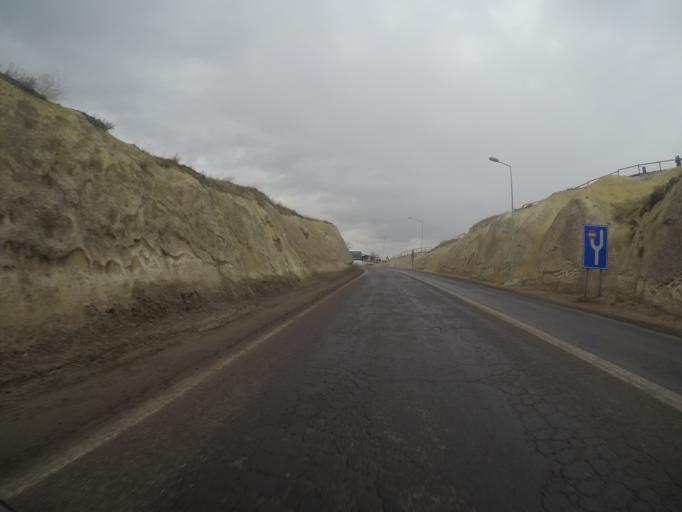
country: TR
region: Nevsehir
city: Urgub
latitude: 38.6346
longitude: 34.8907
